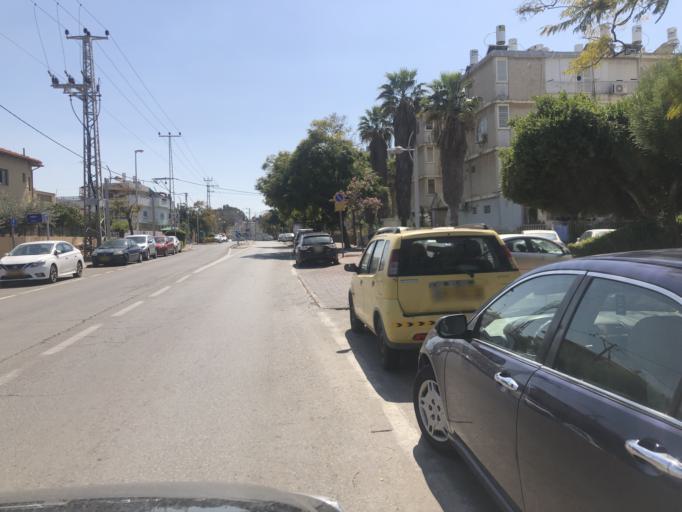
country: IL
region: Tel Aviv
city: Holon
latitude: 32.0085
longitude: 34.7647
